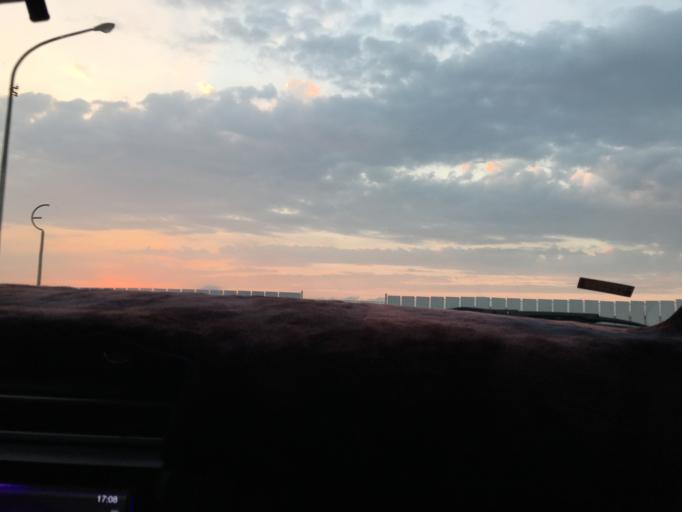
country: TW
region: Taiwan
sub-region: Hsinchu
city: Hsinchu
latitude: 24.8515
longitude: 120.9264
